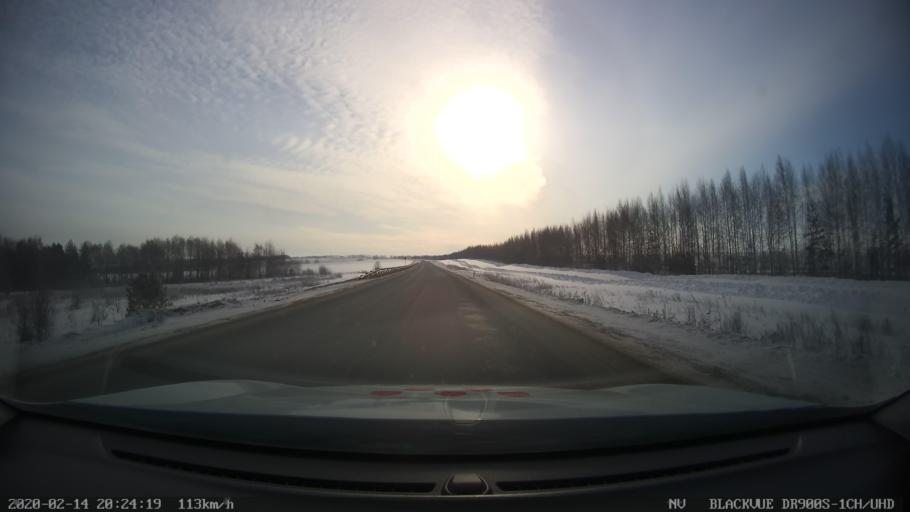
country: RU
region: Tatarstan
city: Verkhniy Uslon
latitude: 55.5144
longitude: 48.9686
